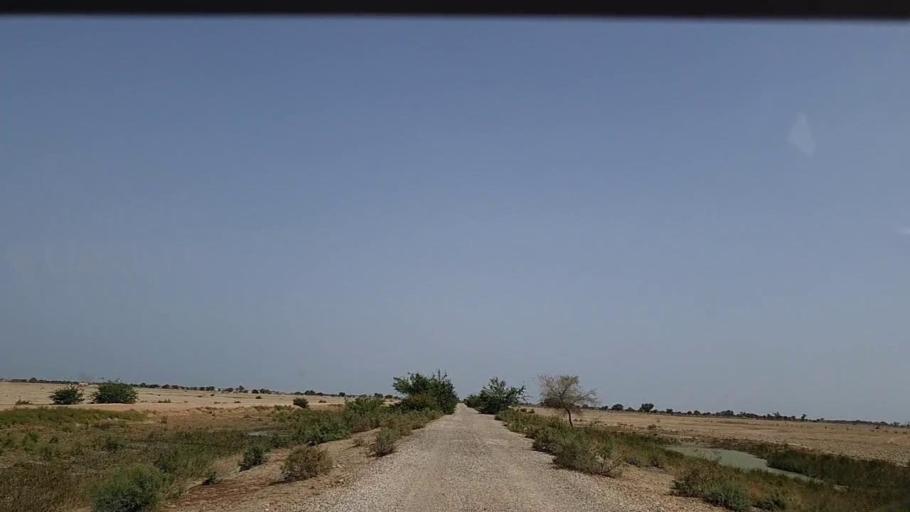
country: PK
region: Sindh
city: Johi
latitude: 26.7602
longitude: 67.6642
